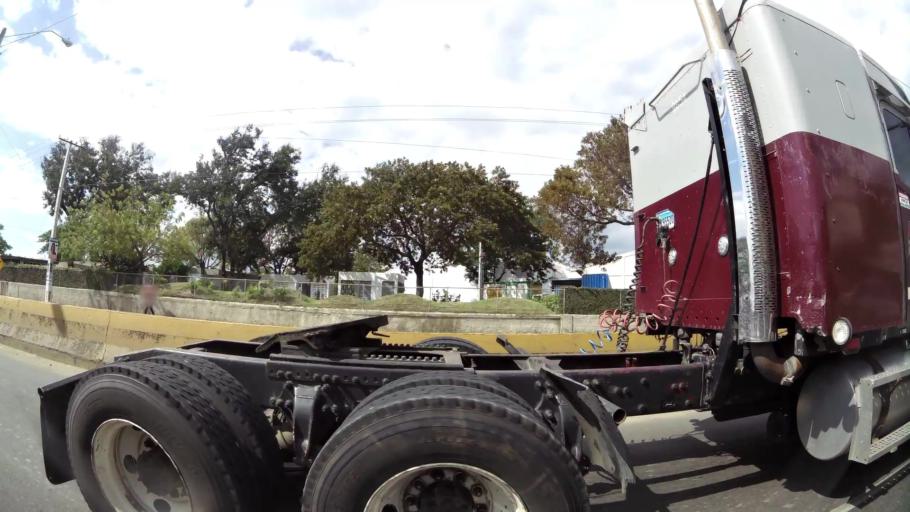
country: DO
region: Santiago
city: Santiago de los Caballeros
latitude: 19.4776
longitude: -70.7245
